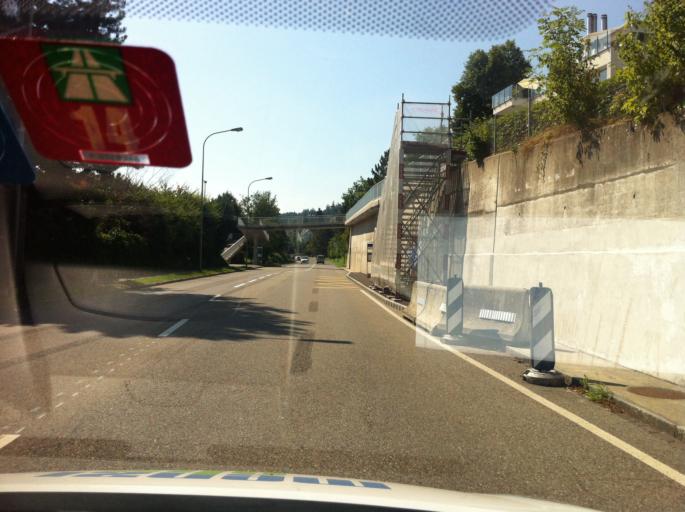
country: CH
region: Zurich
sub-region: Bezirk Horgen
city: Thalwil / Nord
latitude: 47.2950
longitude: 8.5558
